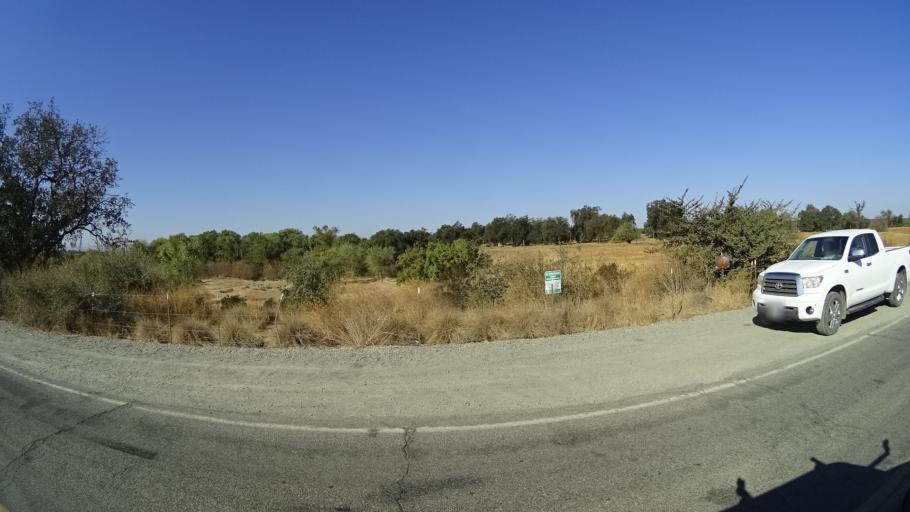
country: US
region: California
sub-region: Yolo County
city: Woodland
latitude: 38.6899
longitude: -121.8654
